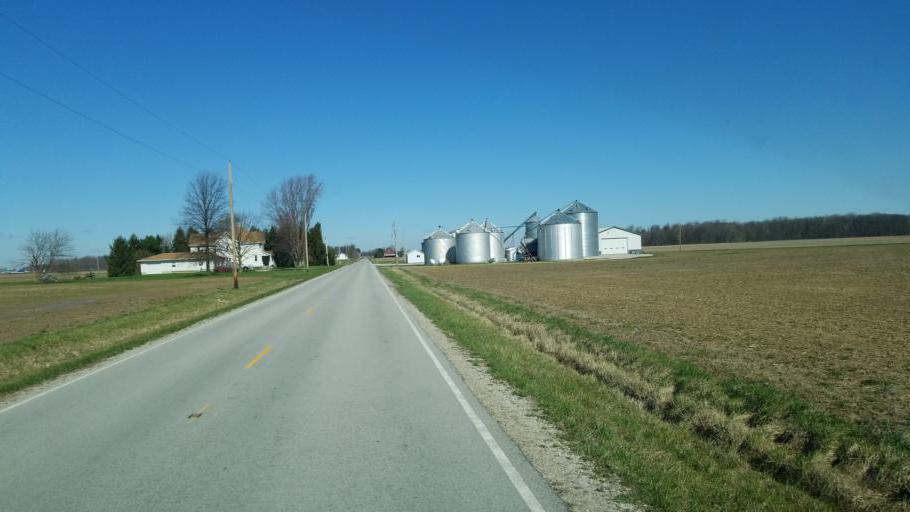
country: US
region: Ohio
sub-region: Huron County
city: Willard
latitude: 41.0347
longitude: -82.8769
